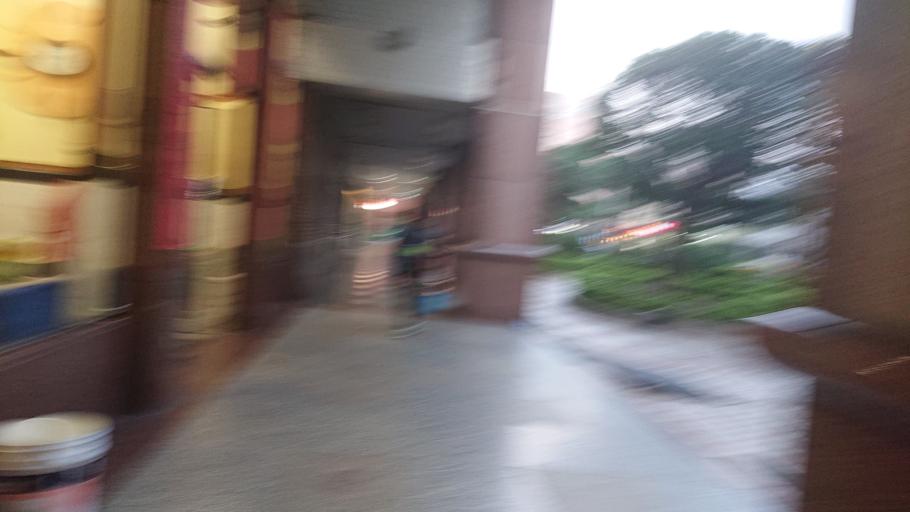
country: TW
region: Taipei
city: Taipei
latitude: 25.1829
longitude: 121.4234
